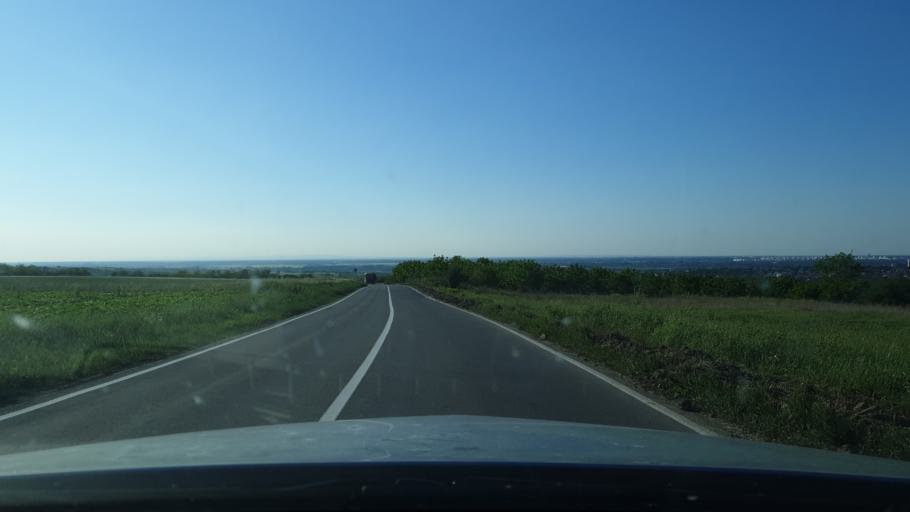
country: RS
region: Central Serbia
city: Sremcica
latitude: 44.7002
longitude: 20.3773
